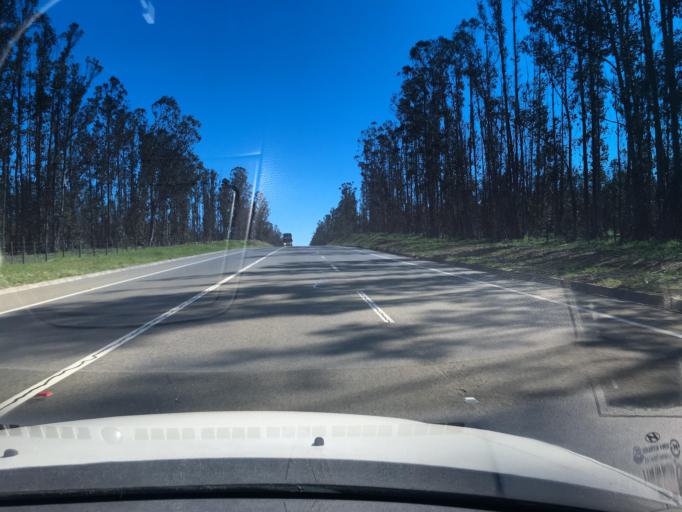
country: CL
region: Valparaiso
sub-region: San Antonio Province
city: El Tabo
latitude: -33.4075
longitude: -71.5573
